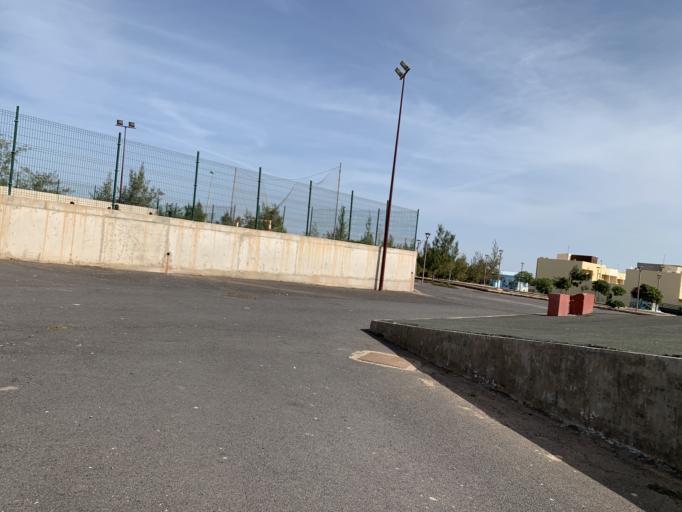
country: ES
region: Canary Islands
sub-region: Provincia de Las Palmas
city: Puerto del Rosario
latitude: 28.5107
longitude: -13.8616
